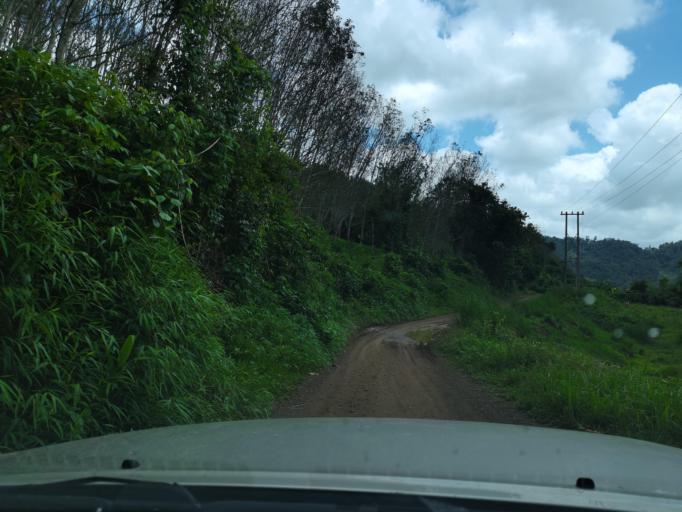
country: LA
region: Loungnamtha
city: Muang Long
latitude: 20.7539
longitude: 101.0179
